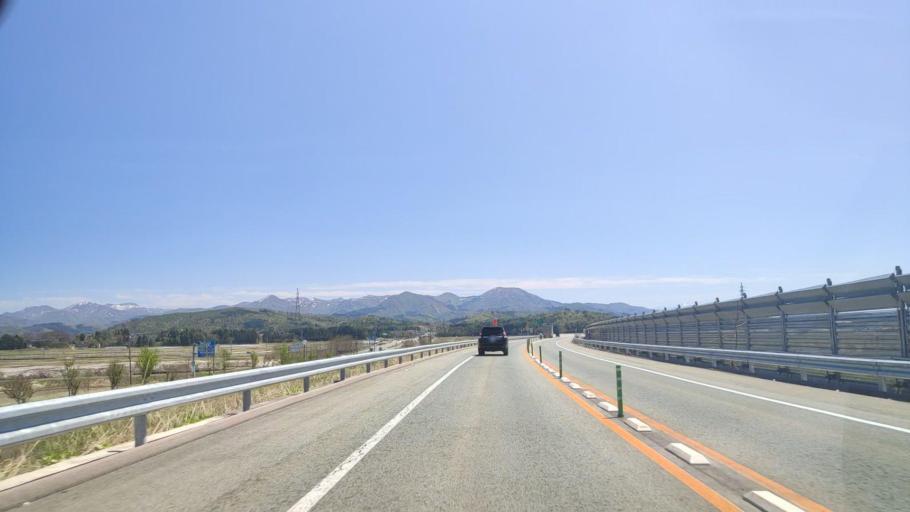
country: JP
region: Yamagata
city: Obanazawa
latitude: 38.6147
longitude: 140.3872
